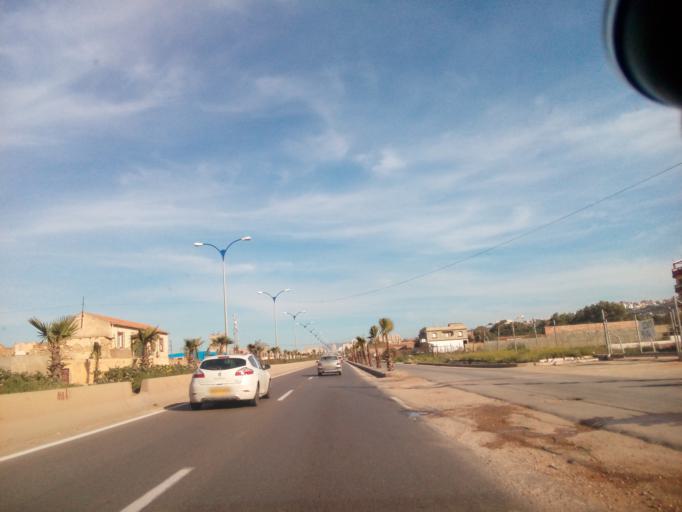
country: DZ
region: Mostaganem
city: Mostaganem
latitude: 35.9090
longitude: 0.0694
